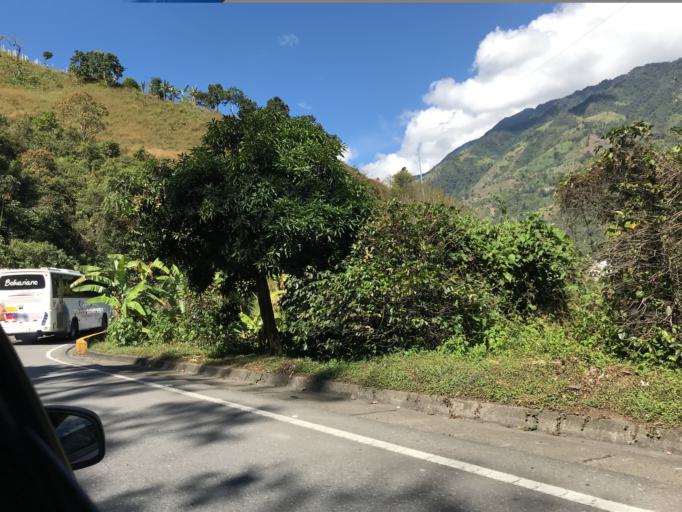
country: CO
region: Tolima
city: Cajamarca
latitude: 4.4412
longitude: -75.4055
